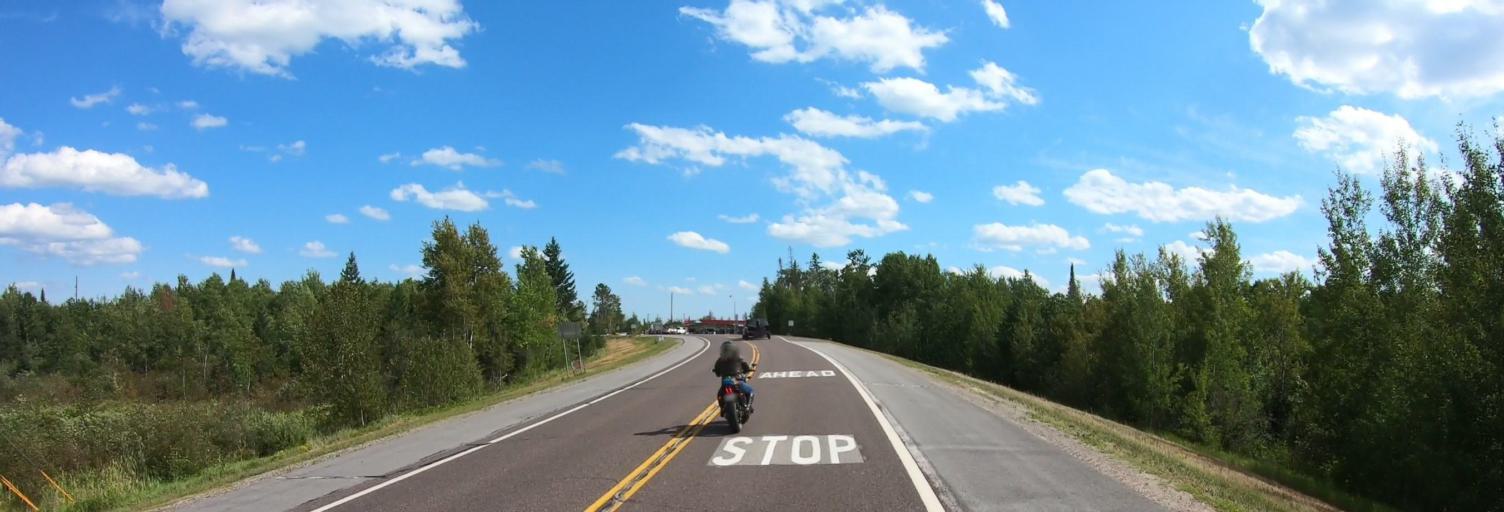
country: US
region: Minnesota
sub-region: Saint Louis County
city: Aurora
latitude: 47.7867
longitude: -92.3652
